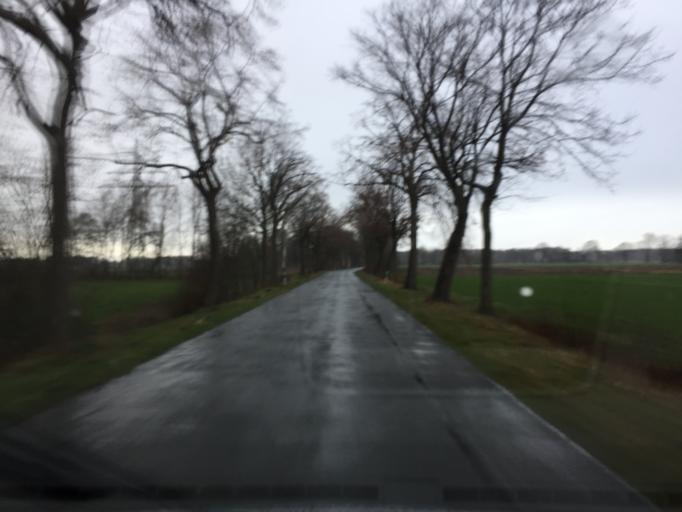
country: DE
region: Lower Saxony
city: Barenburg
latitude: 52.6483
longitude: 8.8210
